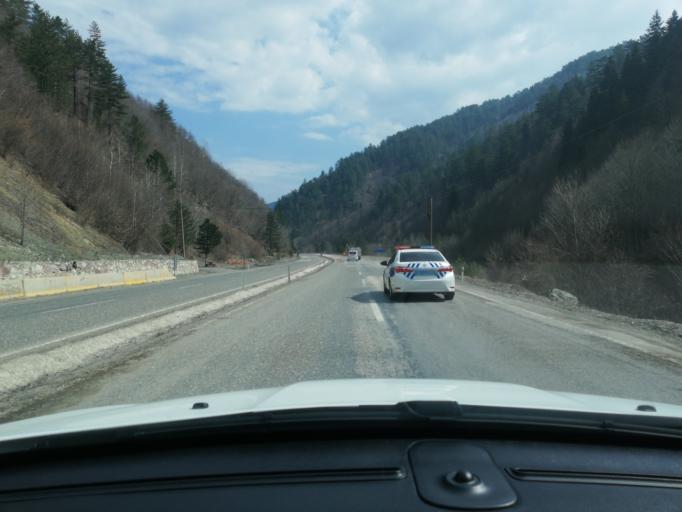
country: TR
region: Kastamonu
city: Kuzyaka
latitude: 41.1225
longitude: 33.7623
